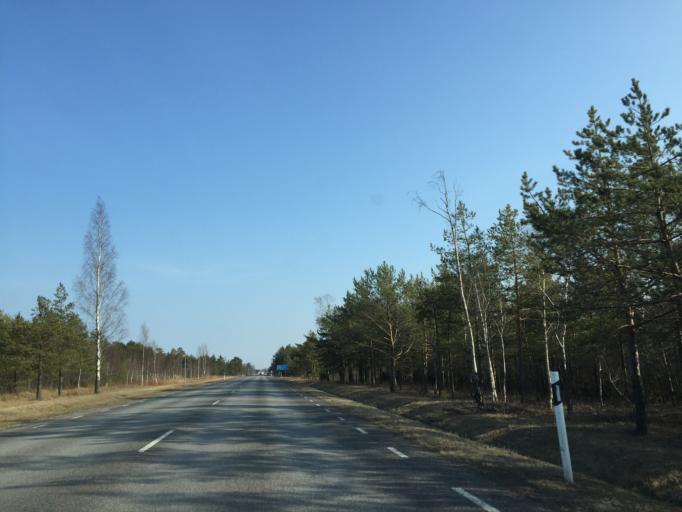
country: EE
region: Saare
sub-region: Orissaare vald
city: Orissaare
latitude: 58.5789
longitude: 23.3630
